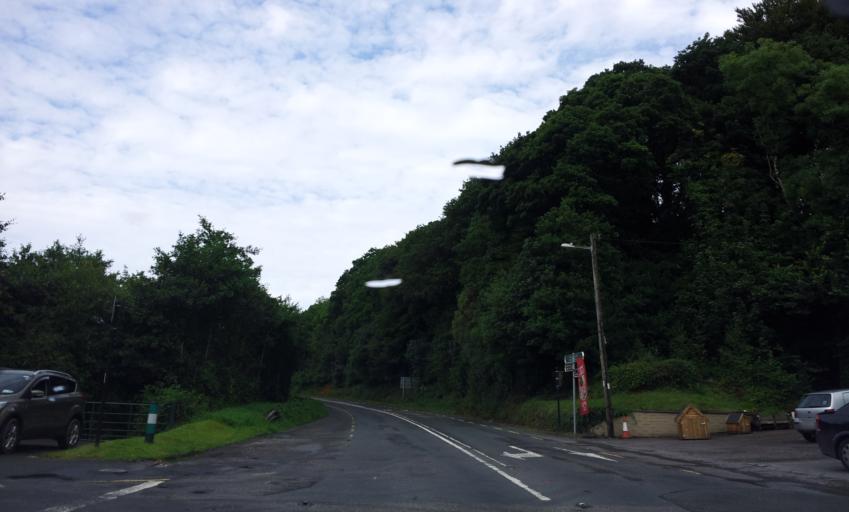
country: IE
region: Munster
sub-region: Ciarrai
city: Cill Airne
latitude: 52.0754
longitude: -9.6314
